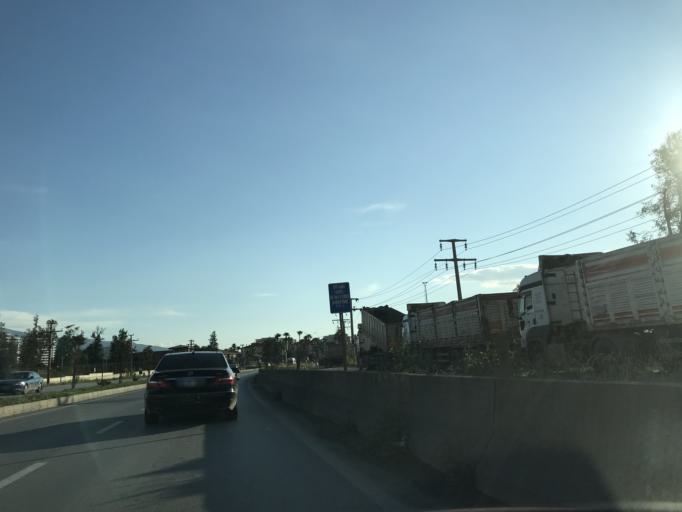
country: TR
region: Hatay
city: Iskenderun
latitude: 36.5921
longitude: 36.1939
